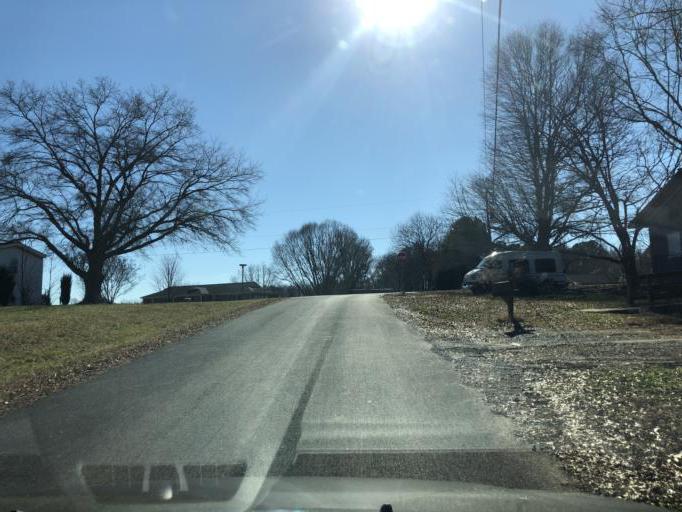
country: US
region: North Carolina
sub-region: Cleveland County
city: Shelby
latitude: 35.2522
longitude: -81.4897
